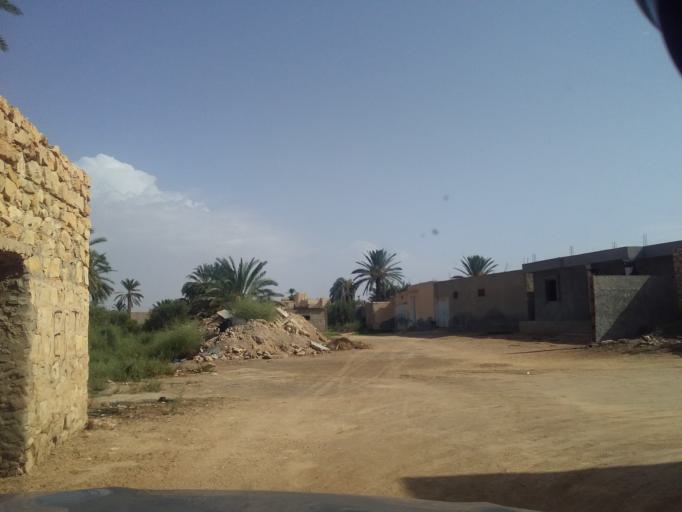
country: TN
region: Qabis
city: Gabes
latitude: 33.6303
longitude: 10.2881
